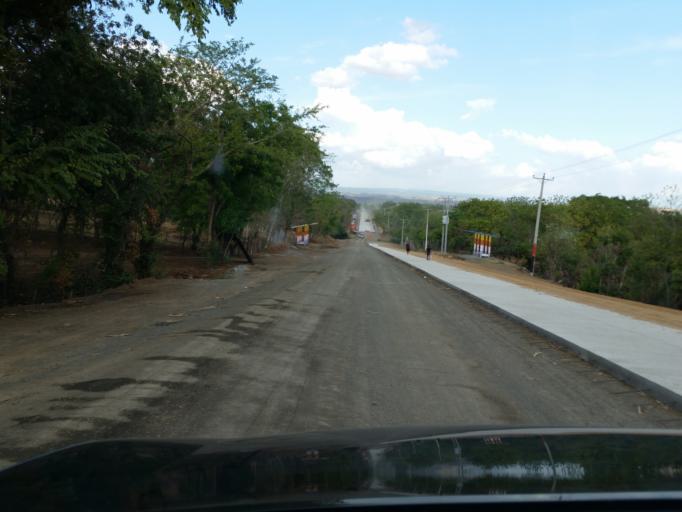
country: NI
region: Managua
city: Carlos Fonseca Amador
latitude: 12.0732
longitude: -86.4955
